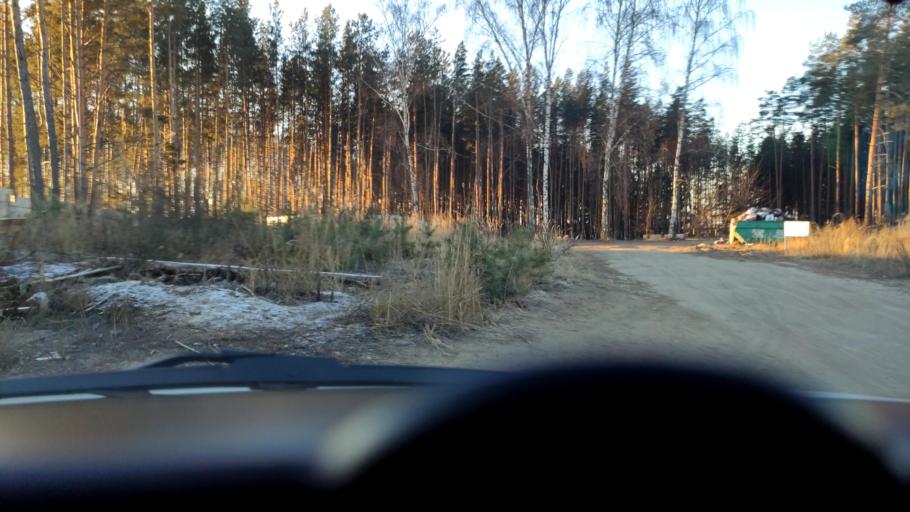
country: RU
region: Voronezj
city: Podgornoye
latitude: 51.7496
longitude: 39.1363
